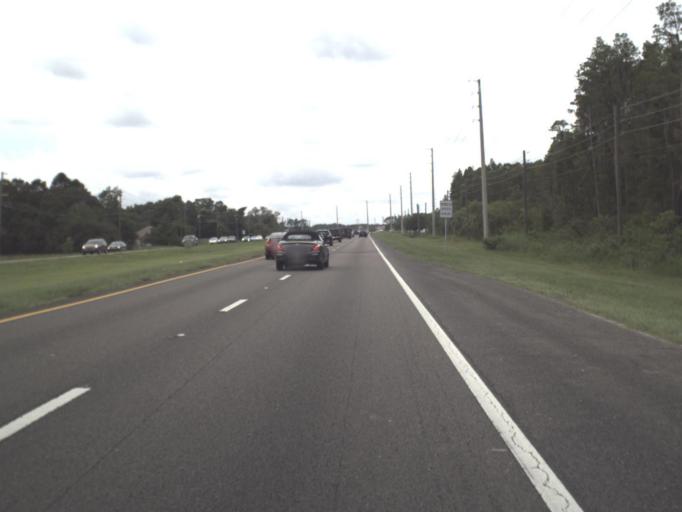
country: US
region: Florida
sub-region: Hillsborough County
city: Cheval
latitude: 28.1946
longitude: -82.5256
